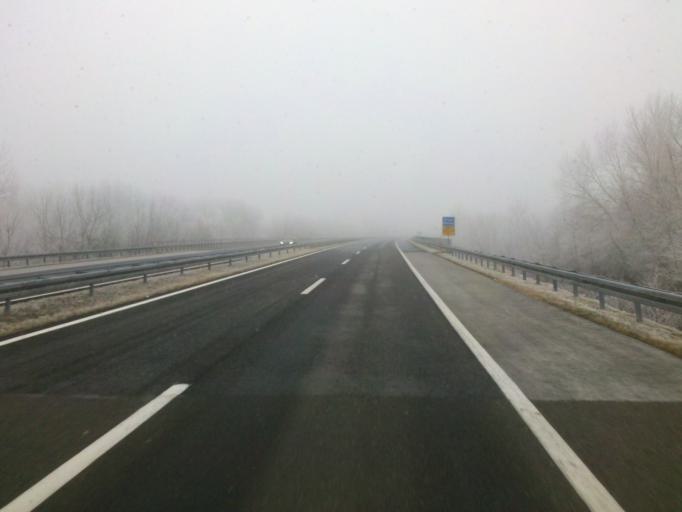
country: HR
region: Medimurska
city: Orehovica
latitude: 46.3066
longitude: 16.5049
